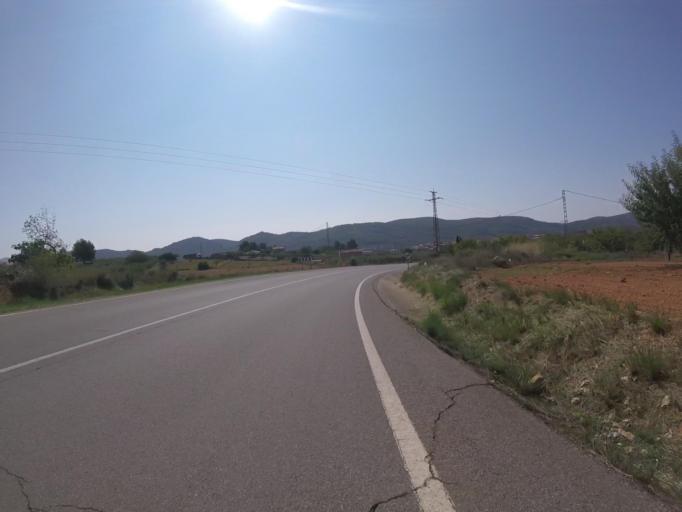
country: ES
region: Valencia
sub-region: Provincia de Castello
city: Adzaneta
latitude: 40.2274
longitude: -0.1738
